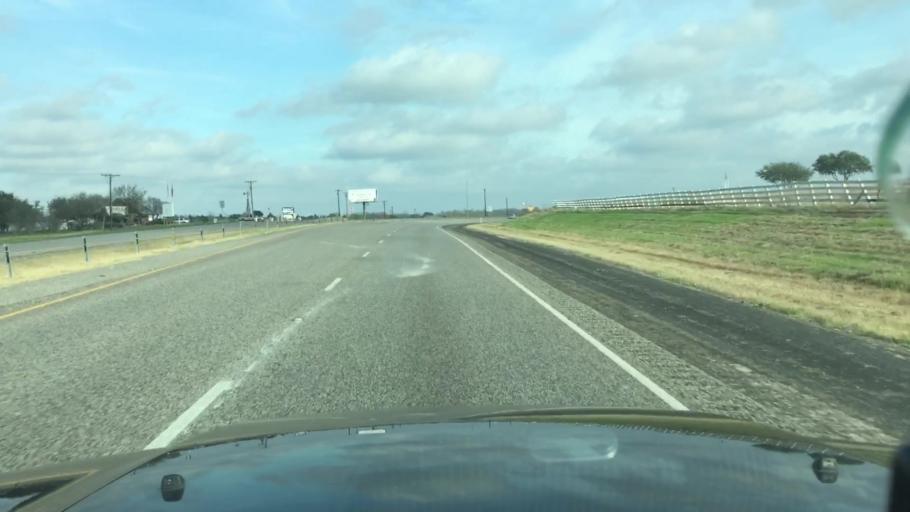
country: US
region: Texas
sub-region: Washington County
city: Brenham
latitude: 30.1412
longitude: -96.2855
